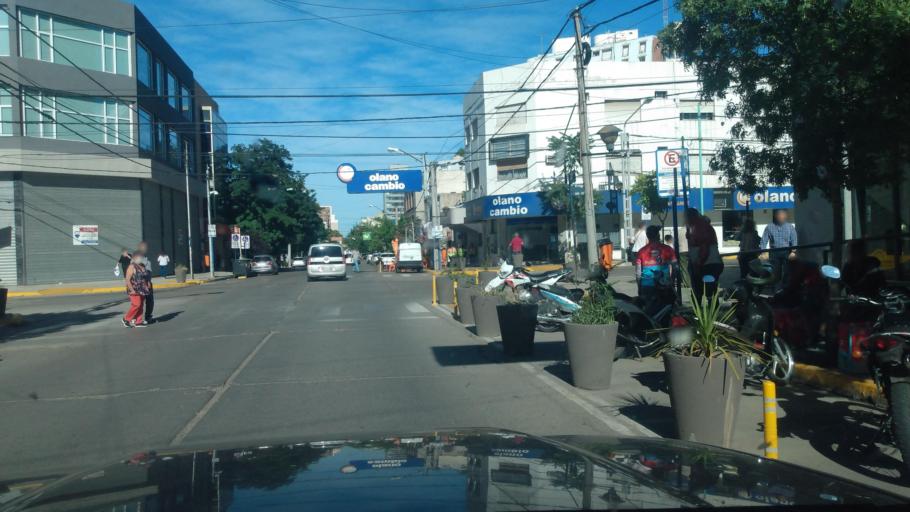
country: AR
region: Neuquen
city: Neuquen
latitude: -38.9540
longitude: -68.0604
